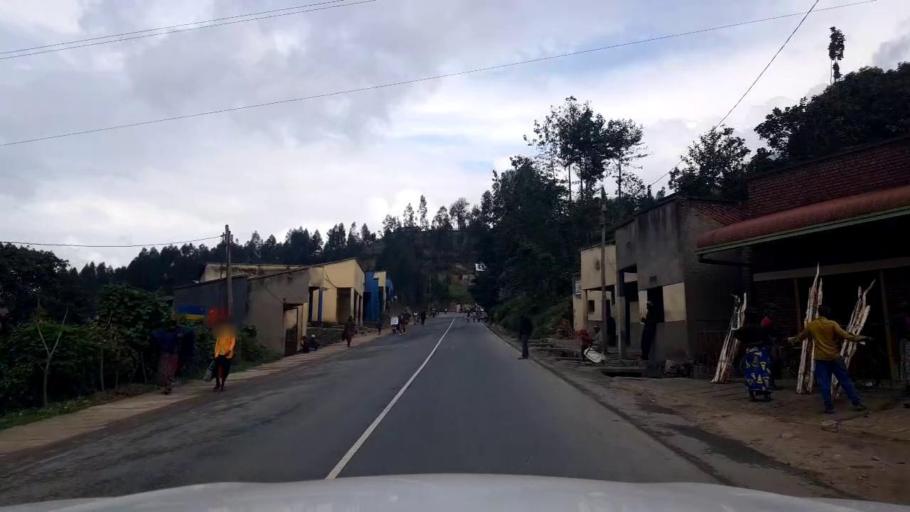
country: RW
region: Northern Province
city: Musanze
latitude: -1.6871
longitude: 29.5171
